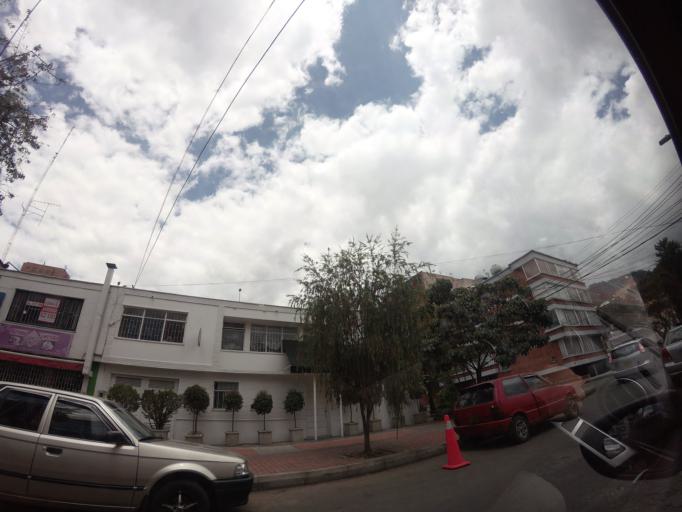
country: CO
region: Bogota D.C.
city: Barrio San Luis
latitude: 4.6629
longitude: -74.0577
